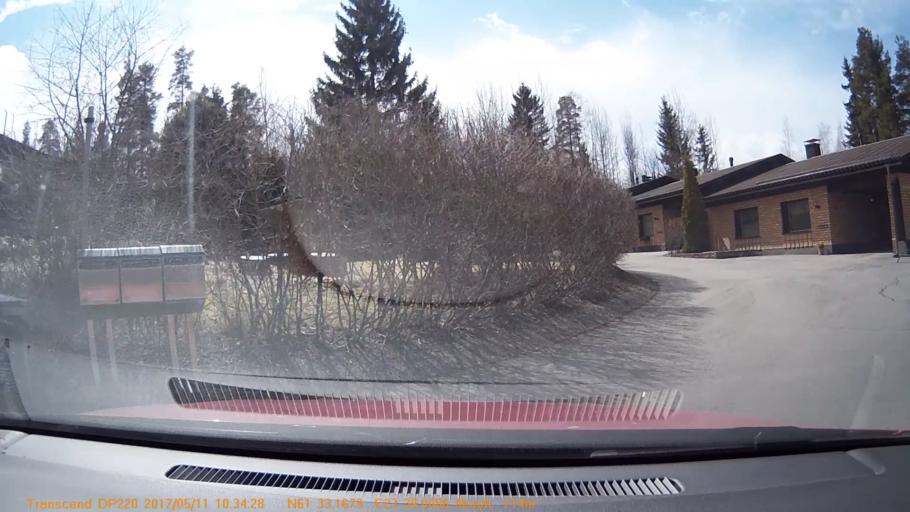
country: FI
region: Pirkanmaa
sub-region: Tampere
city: Yloejaervi
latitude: 61.5528
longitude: 23.6505
